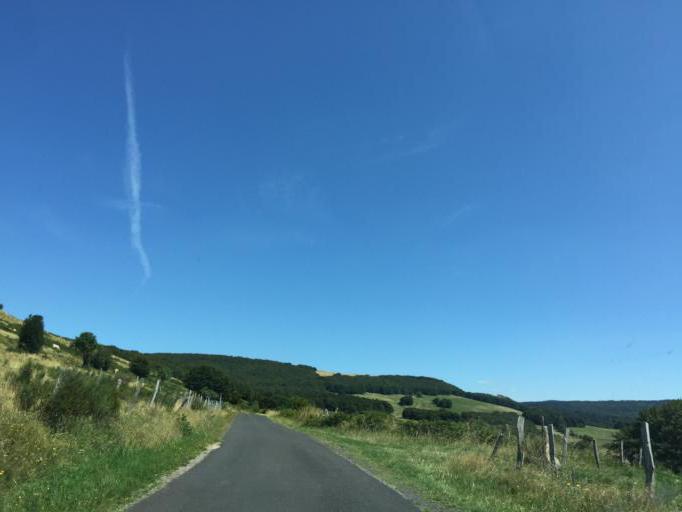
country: FR
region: Midi-Pyrenees
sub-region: Departement de l'Aveyron
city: Laguiole
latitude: 44.6527
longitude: 2.9033
